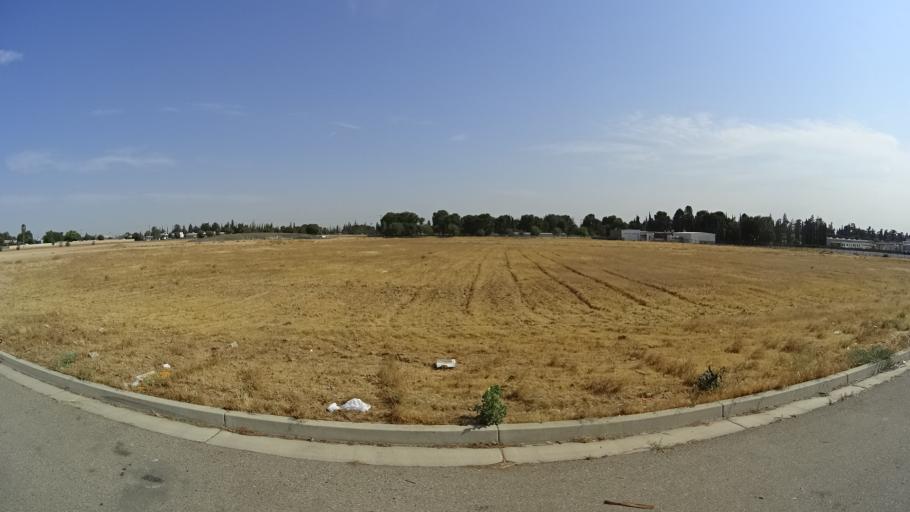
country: US
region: California
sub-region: Fresno County
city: West Park
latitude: 36.7402
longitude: -119.8307
